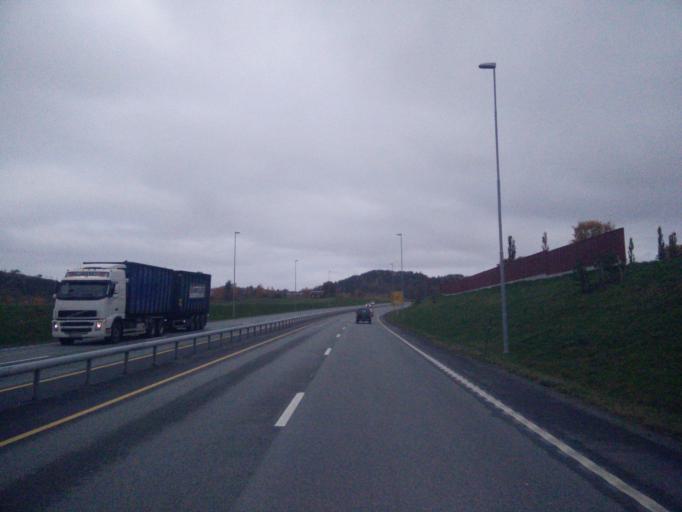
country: NO
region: Nord-Trondelag
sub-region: Stjordal
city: Stjordal
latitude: 63.4833
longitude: 10.8921
